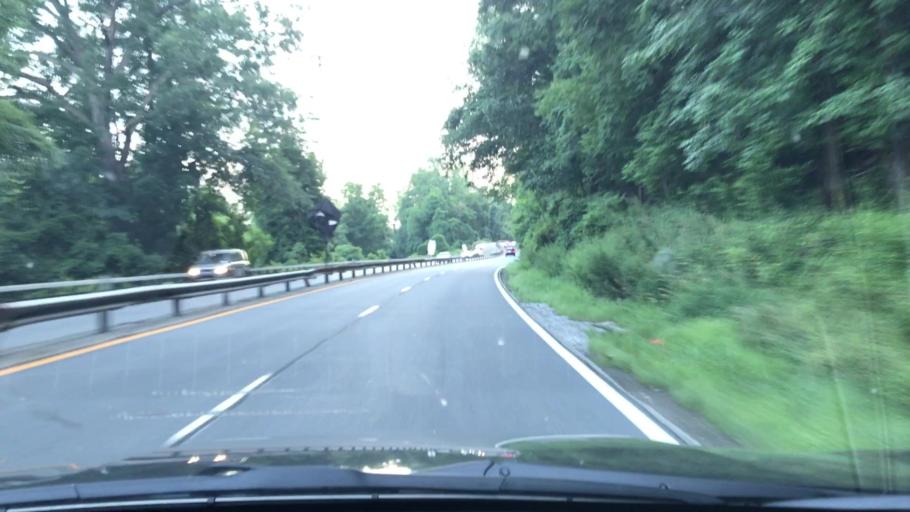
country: US
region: New York
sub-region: Westchester County
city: Greenburgh
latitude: 41.0376
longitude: -73.8391
